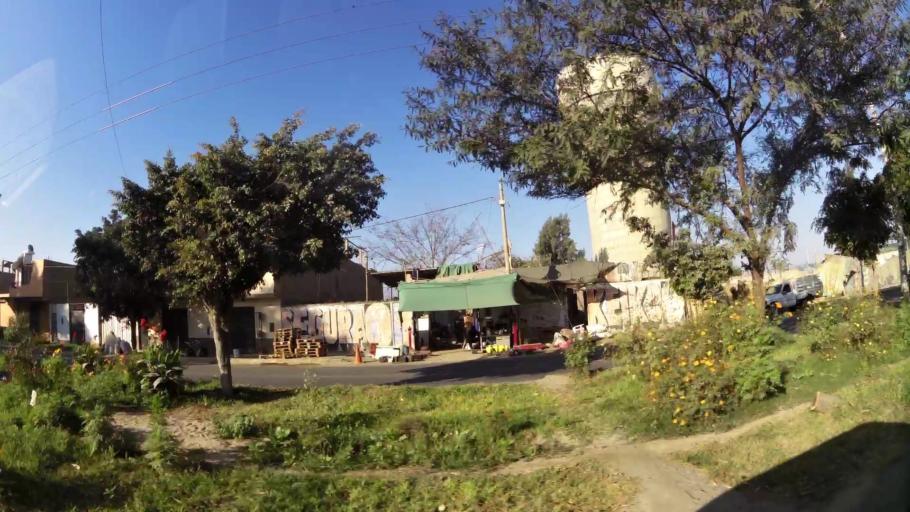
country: PE
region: Ica
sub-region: Provincia de Ica
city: Ica
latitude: -14.0637
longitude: -75.7207
